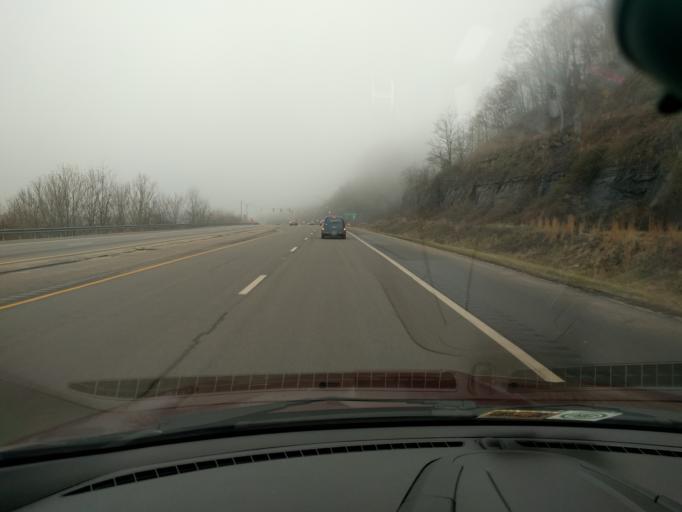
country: US
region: West Virginia
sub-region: Kanawha County
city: Chesapeake
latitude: 38.2097
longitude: -81.5080
